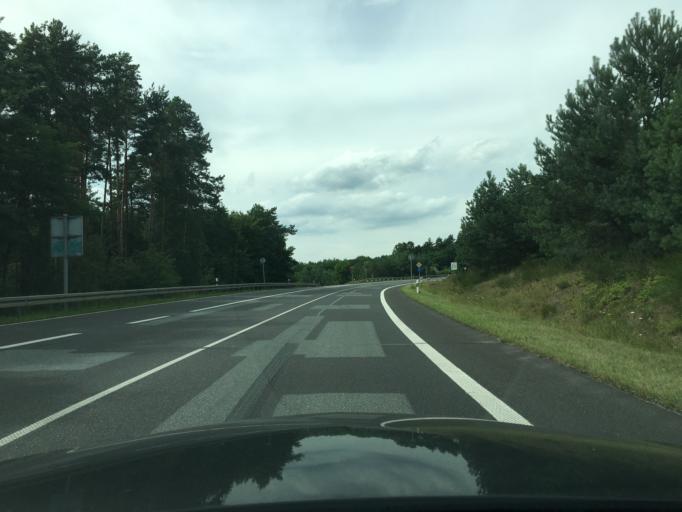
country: DE
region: Mecklenburg-Vorpommern
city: Neustrelitz
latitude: 53.3730
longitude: 13.0812
